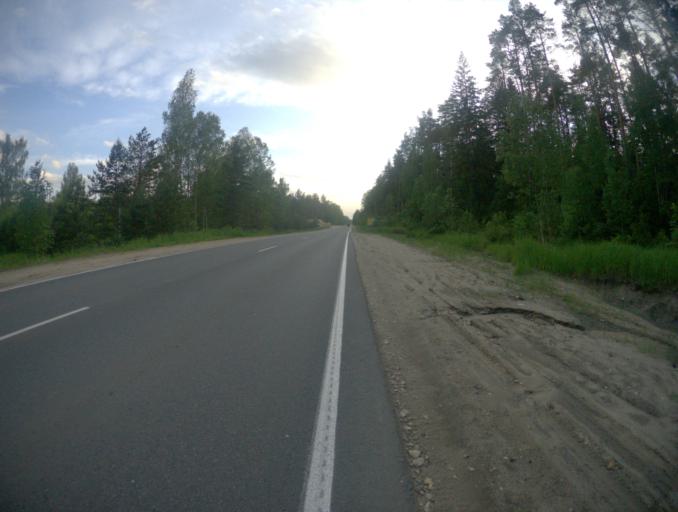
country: RU
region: Vladimir
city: Gus'-Khrustal'nyy
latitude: 55.6374
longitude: 40.7346
